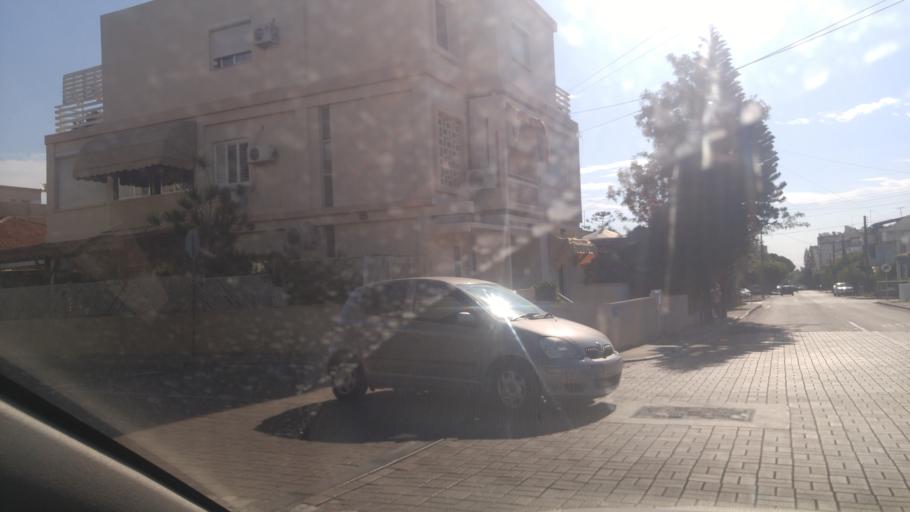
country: CY
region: Limassol
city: Limassol
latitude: 34.6905
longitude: 33.0512
